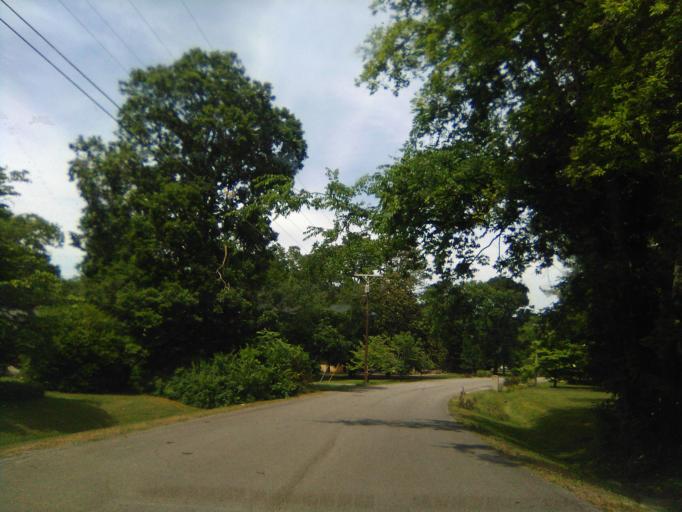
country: US
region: Tennessee
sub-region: Davidson County
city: Belle Meade
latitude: 36.1259
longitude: -86.8968
